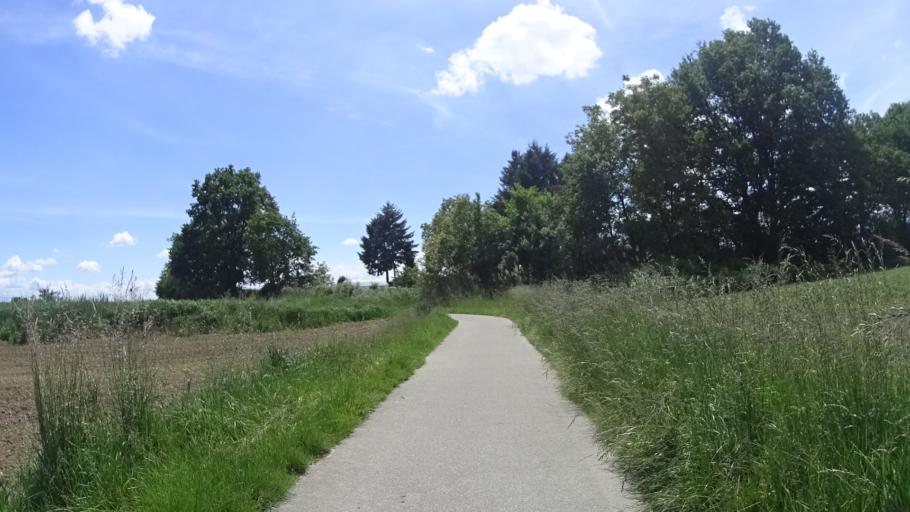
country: DE
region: Baden-Wuerttemberg
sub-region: Freiburg Region
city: Rust
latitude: 48.2798
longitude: 7.7369
